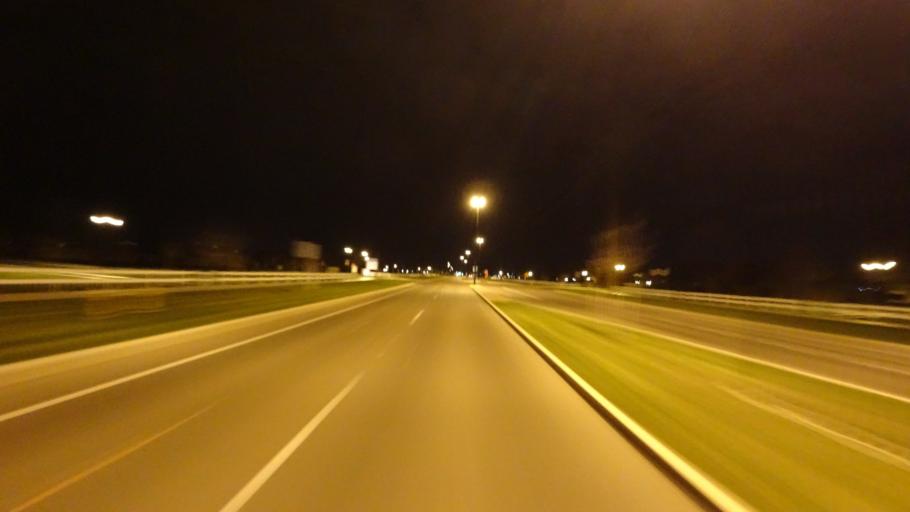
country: US
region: Arizona
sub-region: Maricopa County
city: Gilbert
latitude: 33.3461
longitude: -111.7043
